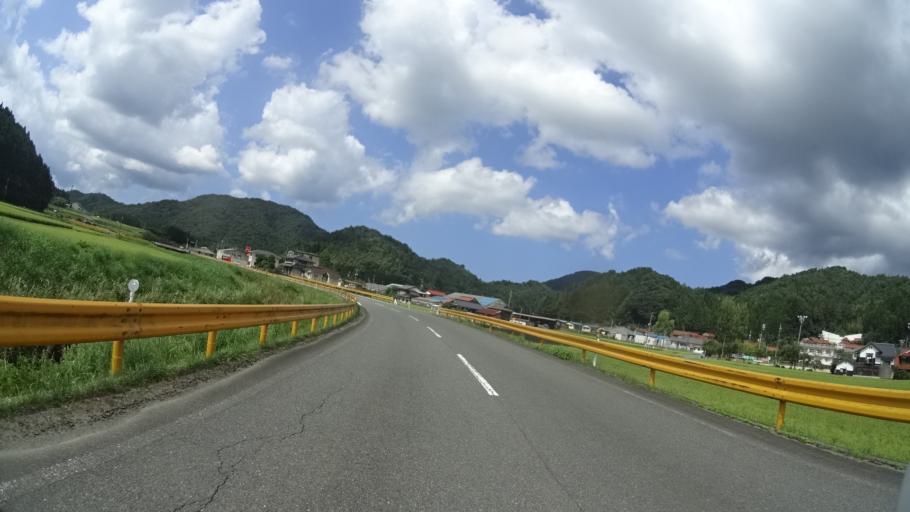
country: JP
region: Yamaguchi
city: Hagi
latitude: 34.5154
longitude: 131.6008
